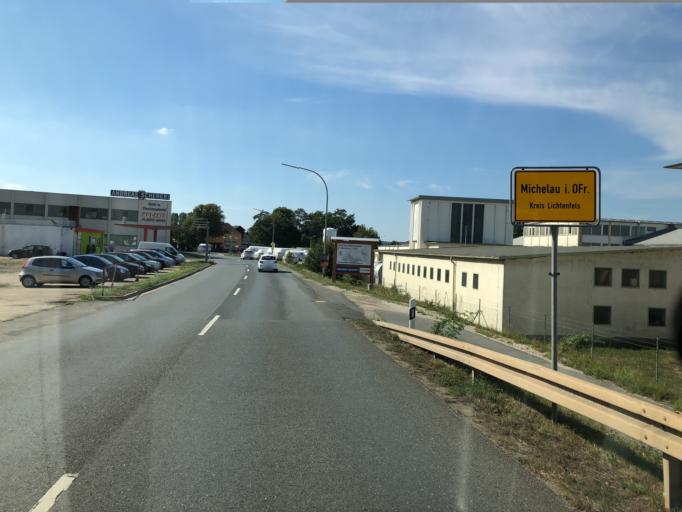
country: DE
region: Bavaria
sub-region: Upper Franconia
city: Michelau
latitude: 50.1555
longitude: 11.1188
